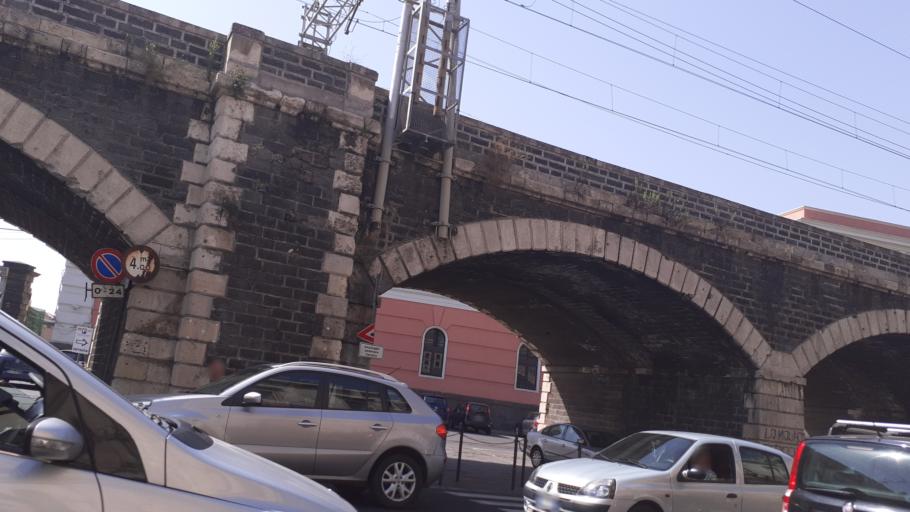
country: IT
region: Sicily
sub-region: Catania
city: Catania
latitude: 37.5015
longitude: 15.0937
